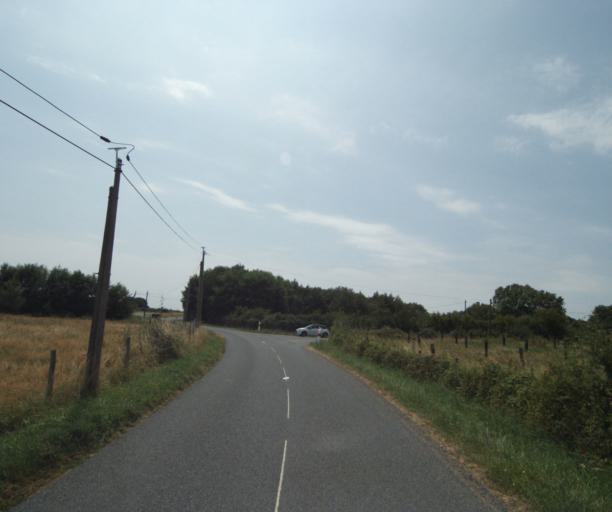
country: FR
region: Bourgogne
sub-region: Departement de Saone-et-Loire
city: Gueugnon
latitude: 46.5842
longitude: 4.0483
